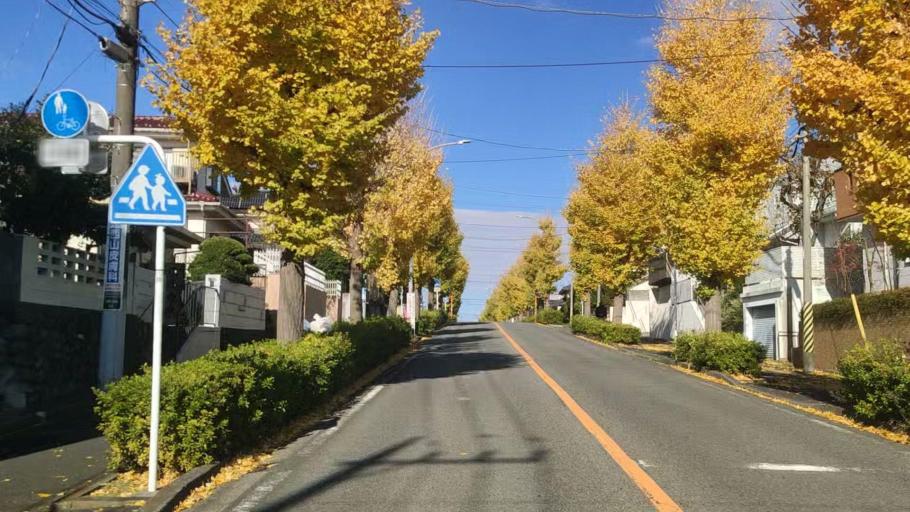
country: JP
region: Kanagawa
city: Minami-rinkan
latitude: 35.4553
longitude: 139.5349
